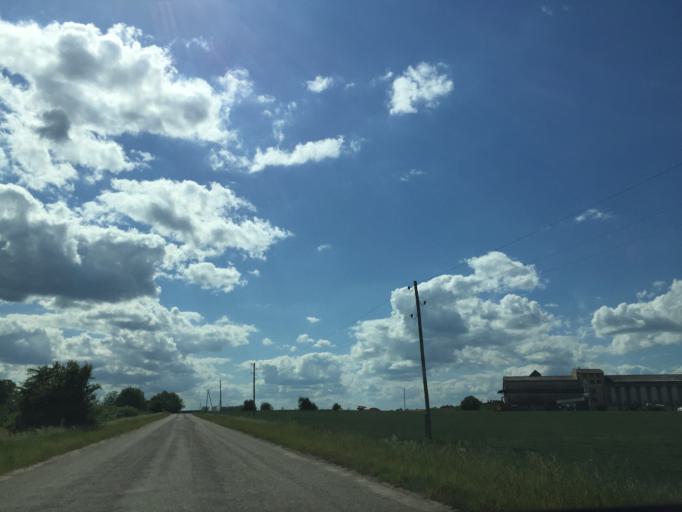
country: LV
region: Engure
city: Smarde
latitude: 56.8579
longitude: 23.3110
